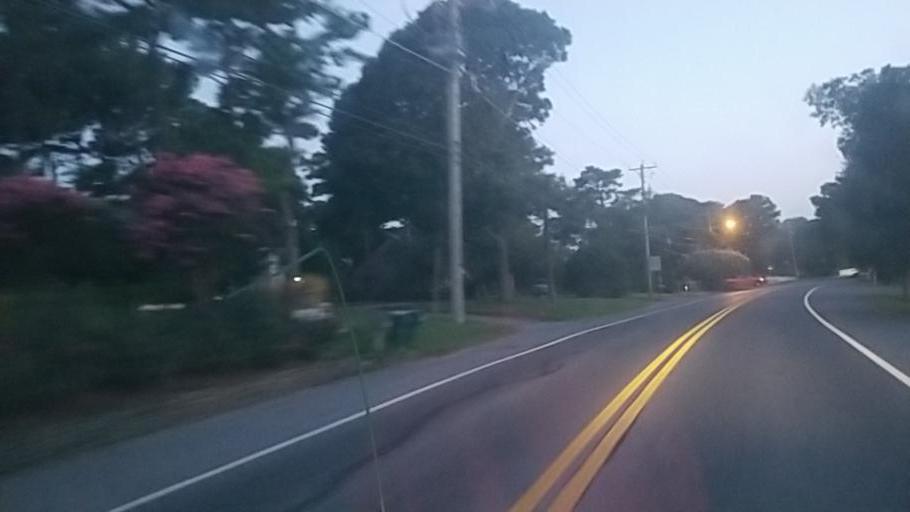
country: US
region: Delaware
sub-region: Sussex County
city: Rehoboth Beach
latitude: 38.7061
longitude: -75.0803
